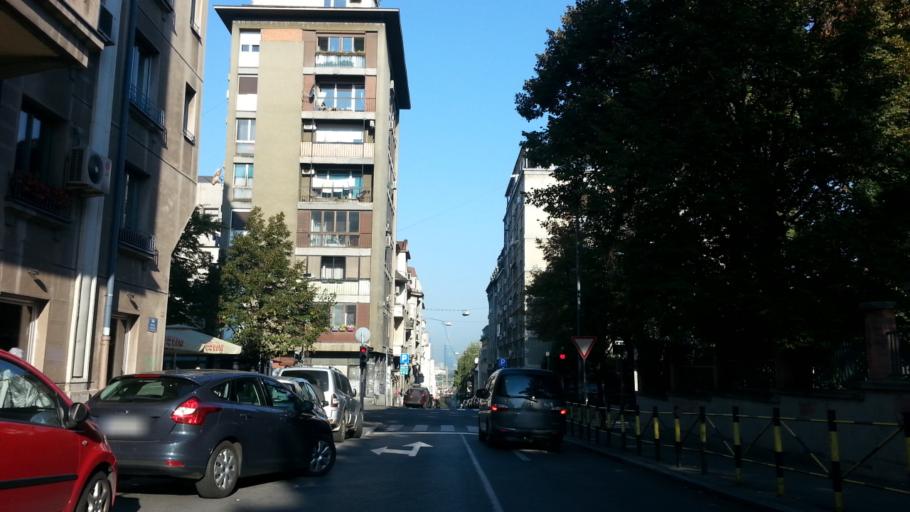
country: RS
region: Central Serbia
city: Belgrade
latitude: 44.8024
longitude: 20.4600
